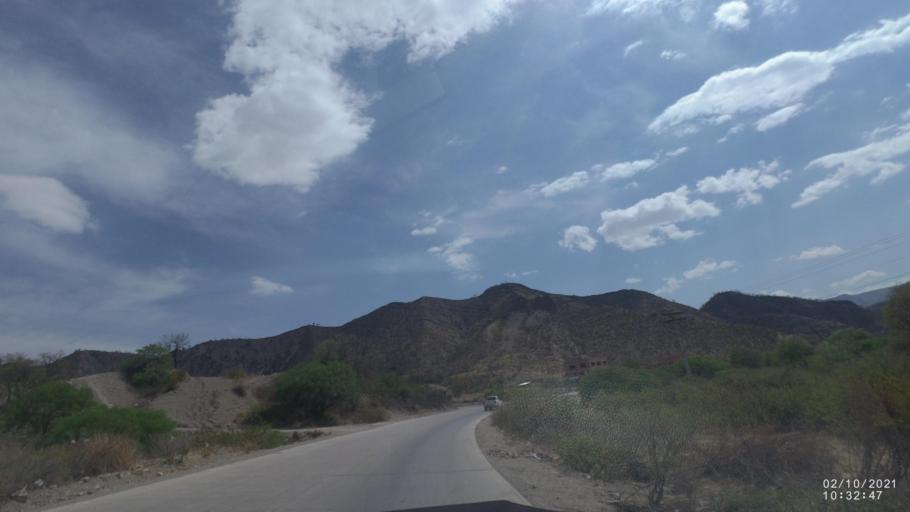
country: BO
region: Cochabamba
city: Capinota
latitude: -17.6852
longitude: -66.2600
